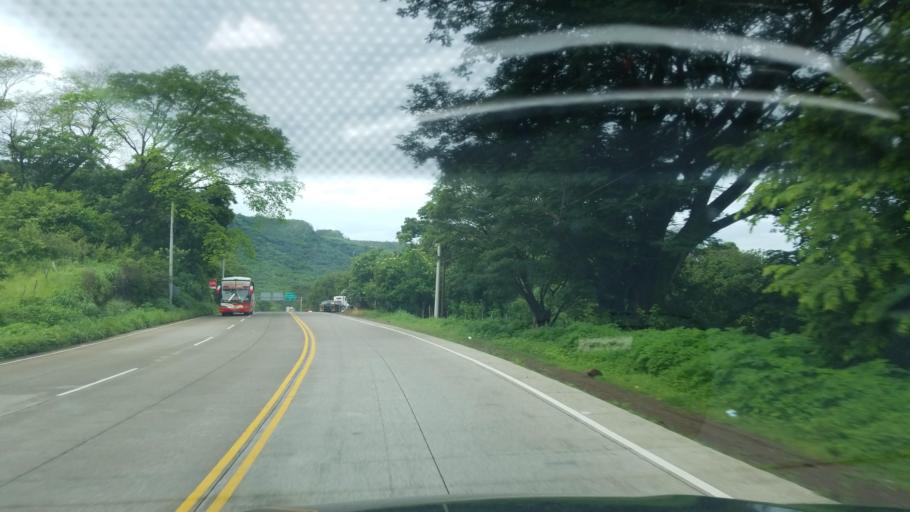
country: HN
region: Francisco Morazan
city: El Porvenir
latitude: 13.6938
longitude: -87.3288
